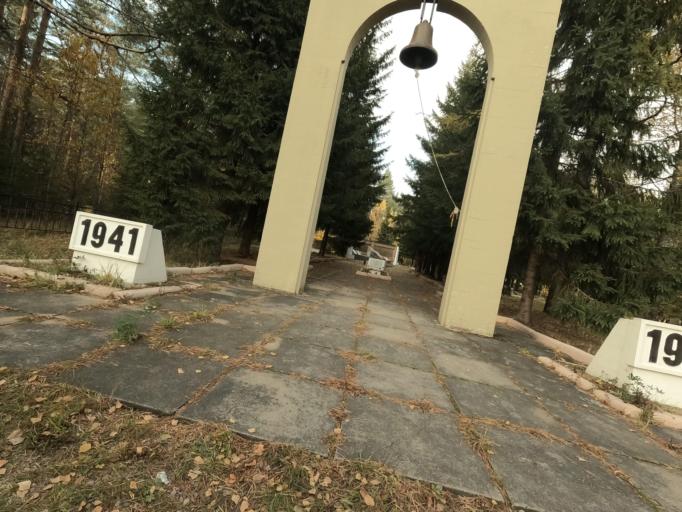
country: RU
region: Leningrad
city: Priladozhskiy
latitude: 59.6361
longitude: 31.4059
